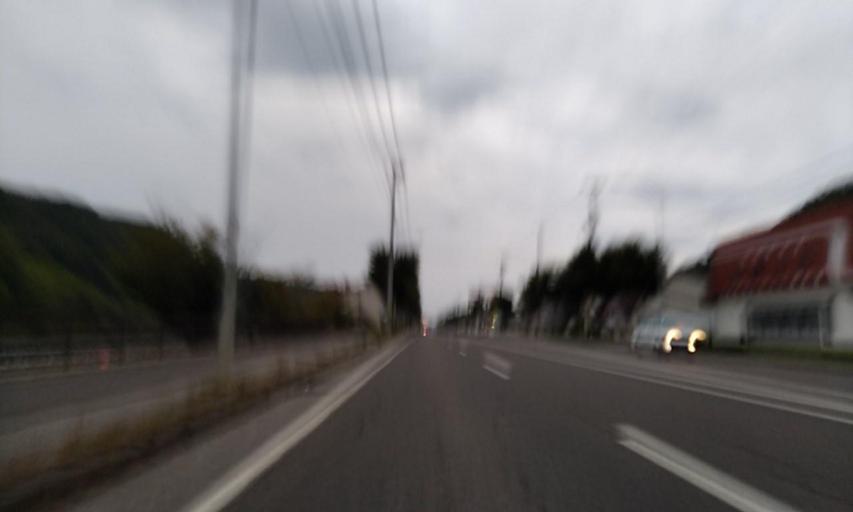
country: JP
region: Hokkaido
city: Abashiri
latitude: 44.0157
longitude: 144.2409
